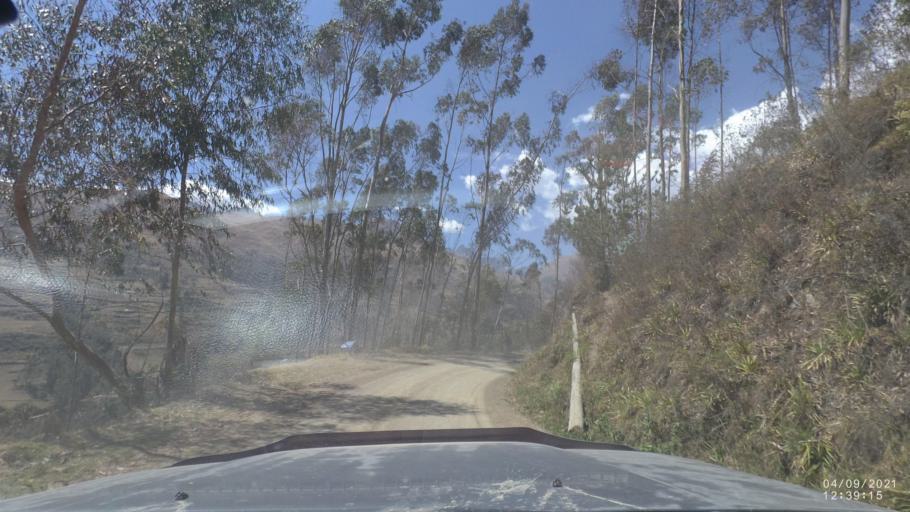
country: BO
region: Cochabamba
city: Colchani
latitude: -17.2291
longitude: -66.4995
